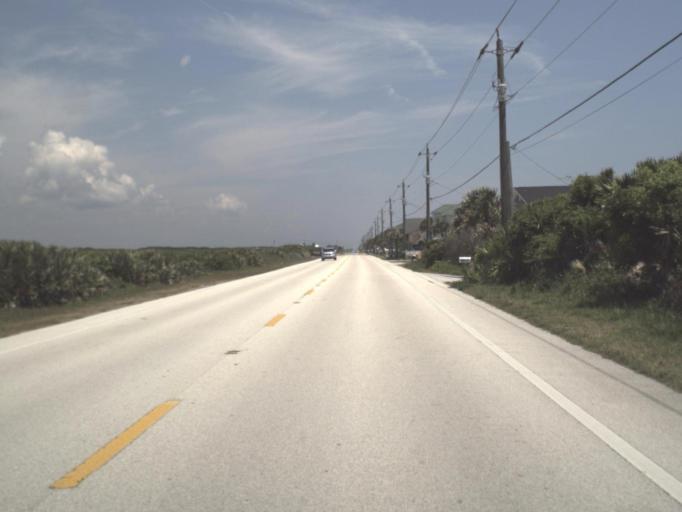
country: US
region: Florida
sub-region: Saint Johns County
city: Villano Beach
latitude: 30.0136
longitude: -81.3210
